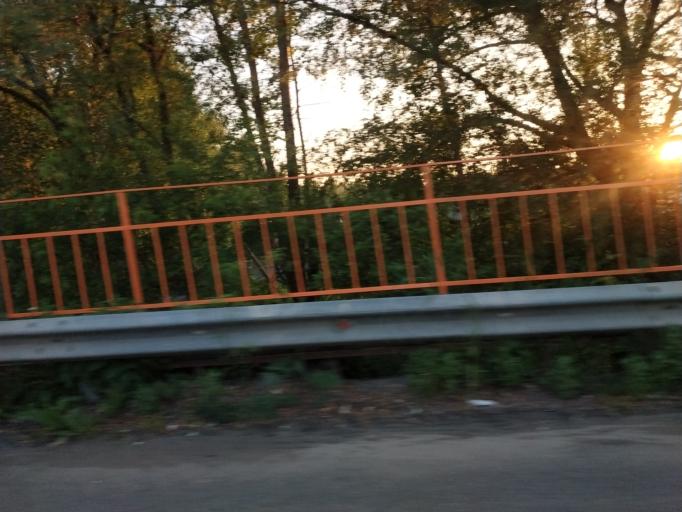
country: RU
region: Moskovskaya
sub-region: Shchelkovskiy Rayon
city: Grebnevo
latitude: 55.9918
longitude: 38.1277
